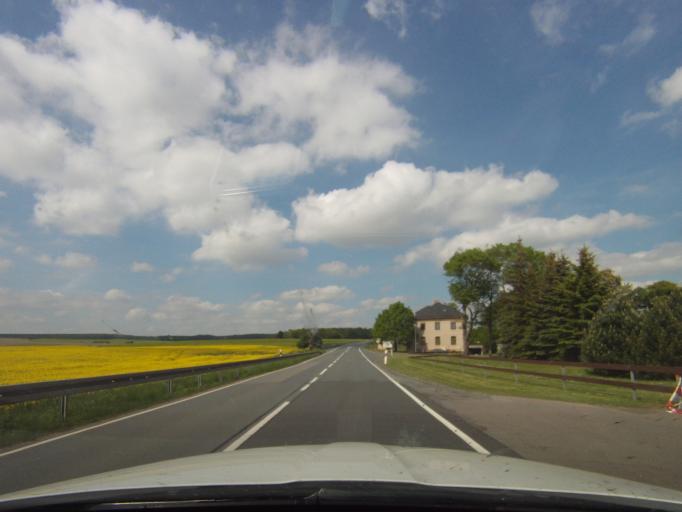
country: DE
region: Thuringia
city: Mittelpollnitz
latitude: 50.7652
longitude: 11.9253
